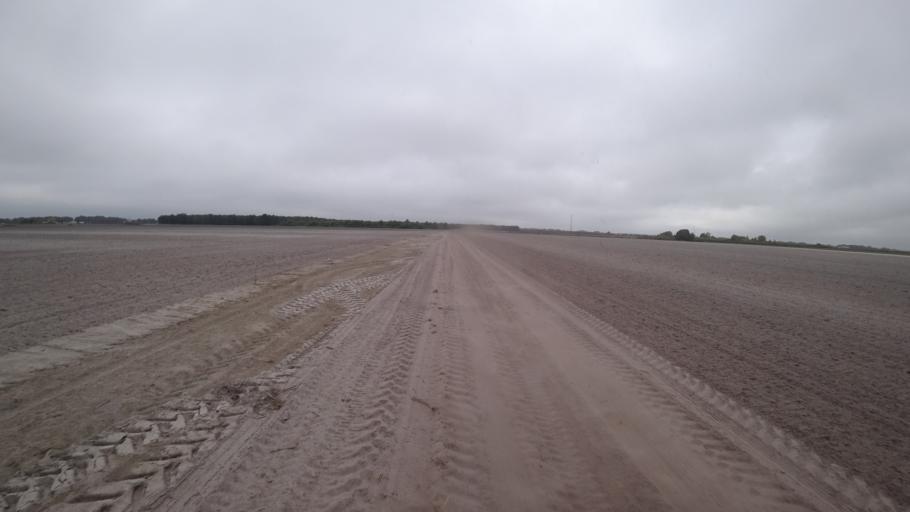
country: US
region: Florida
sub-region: Sarasota County
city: Warm Mineral Springs
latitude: 27.2879
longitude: -82.1754
